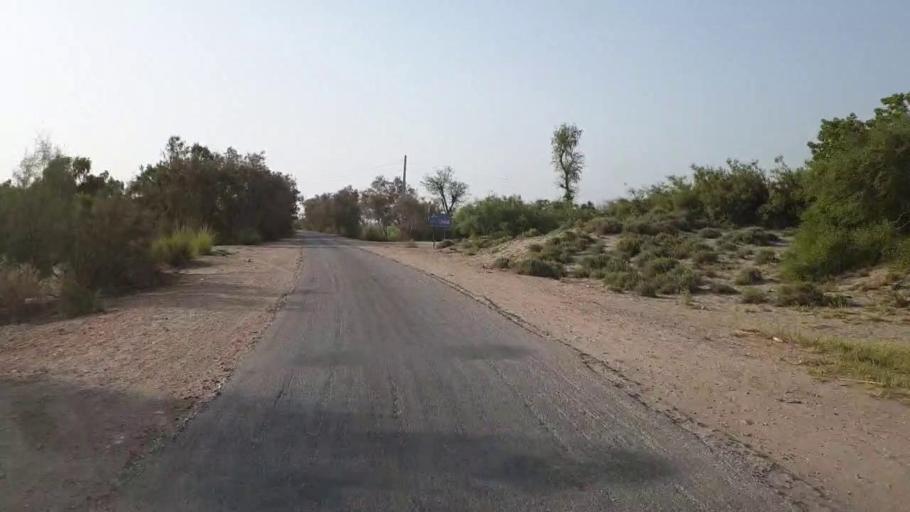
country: PK
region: Sindh
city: Jam Sahib
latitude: 26.4876
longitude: 68.8606
